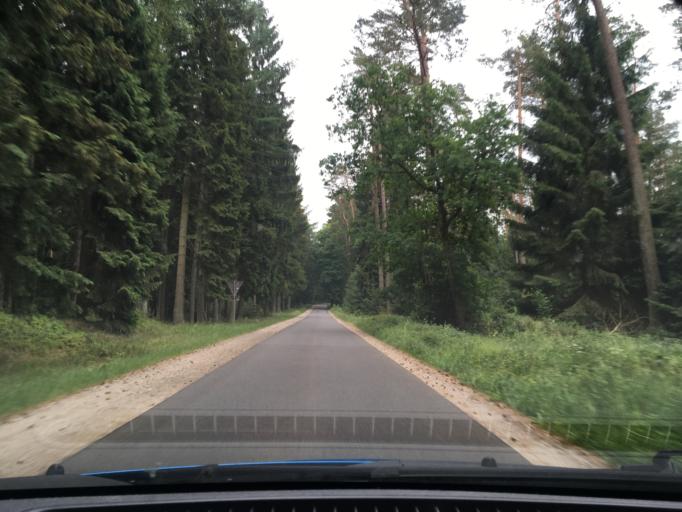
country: DE
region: Lower Saxony
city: Gohrde
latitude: 53.1189
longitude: 10.8613
